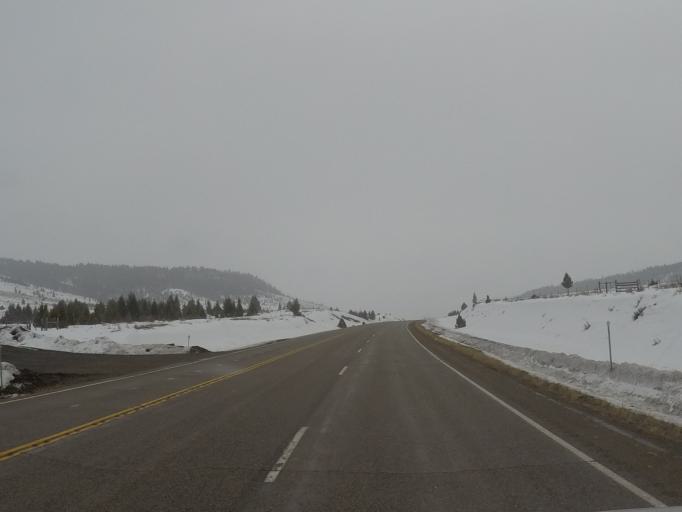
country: US
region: Montana
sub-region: Meagher County
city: White Sulphur Springs
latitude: 46.6635
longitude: -110.8751
